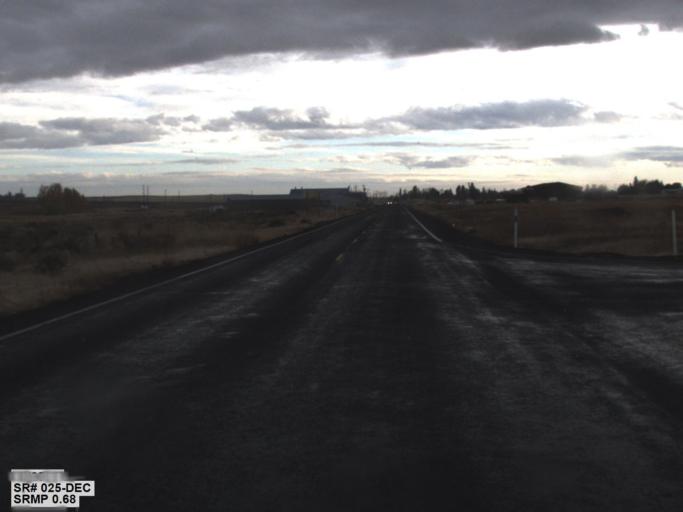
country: US
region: Washington
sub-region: Lincoln County
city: Davenport
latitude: 47.6647
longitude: -118.1410
